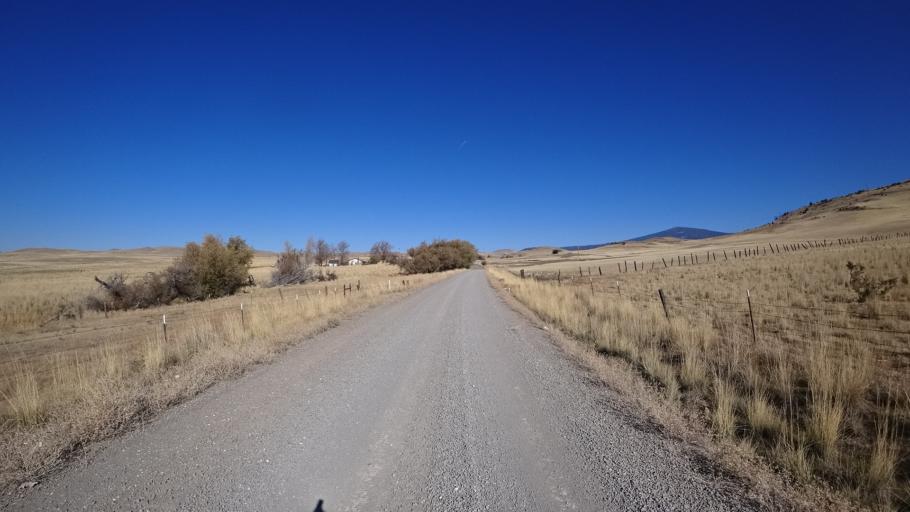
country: US
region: California
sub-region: Siskiyou County
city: Montague
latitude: 41.7404
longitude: -122.3671
